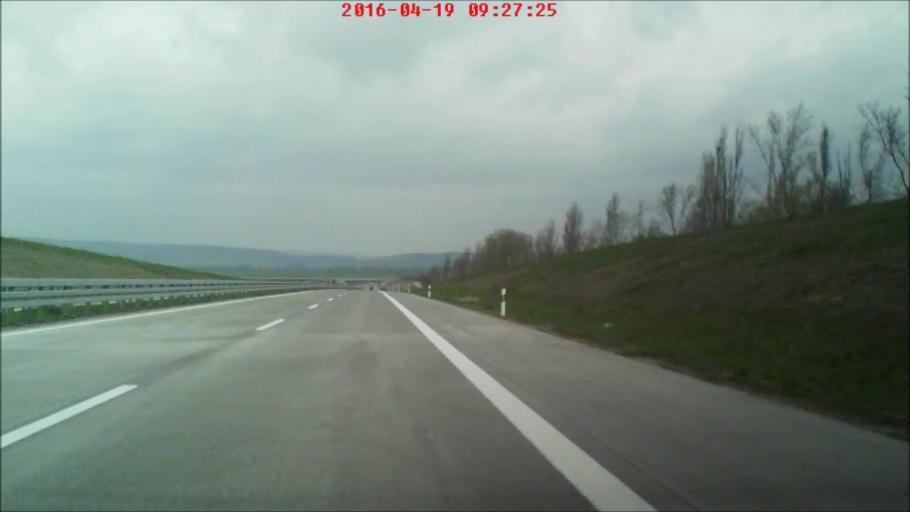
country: DE
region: Thuringia
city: Schillingstedt
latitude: 51.2167
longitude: 11.1847
